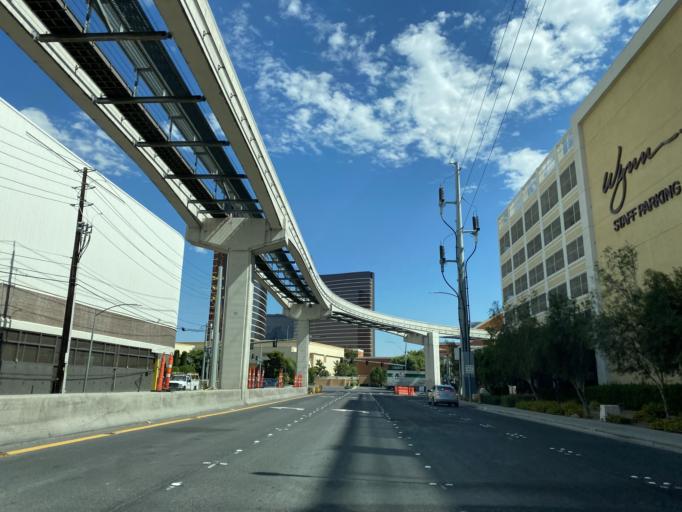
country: US
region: Nevada
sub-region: Clark County
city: Paradise
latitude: 36.1213
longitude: -115.1640
